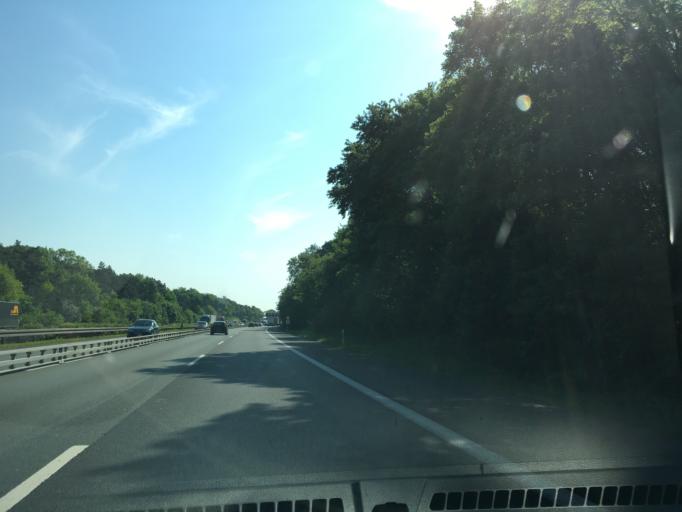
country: DE
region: Lower Saxony
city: Garbsen
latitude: 52.4205
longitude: 9.5389
